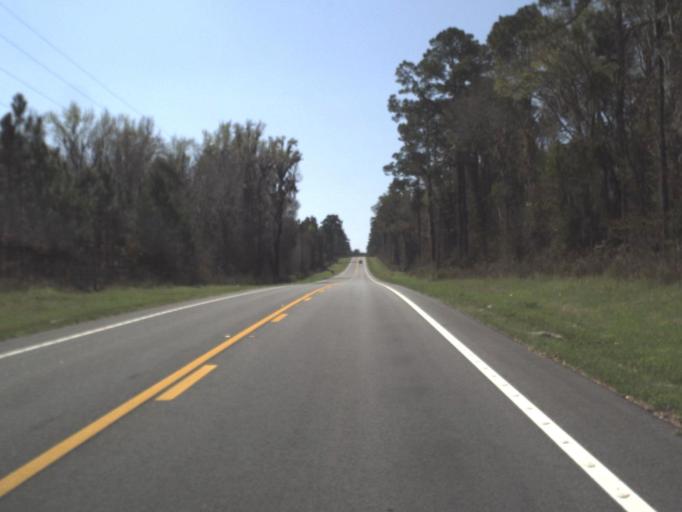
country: US
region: Florida
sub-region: Jefferson County
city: Monticello
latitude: 30.4200
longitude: -84.0203
